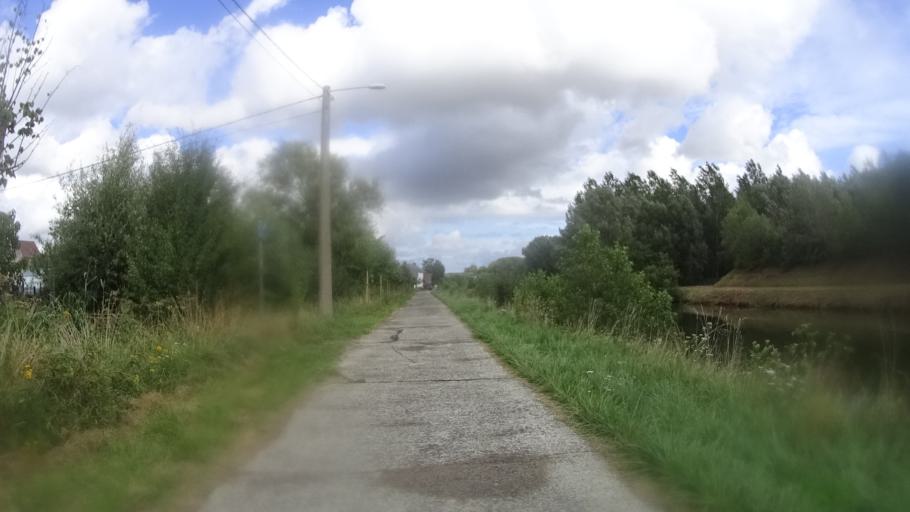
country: BE
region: Wallonia
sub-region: Province du Hainaut
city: Erquelinnes
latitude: 50.3089
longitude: 4.1341
